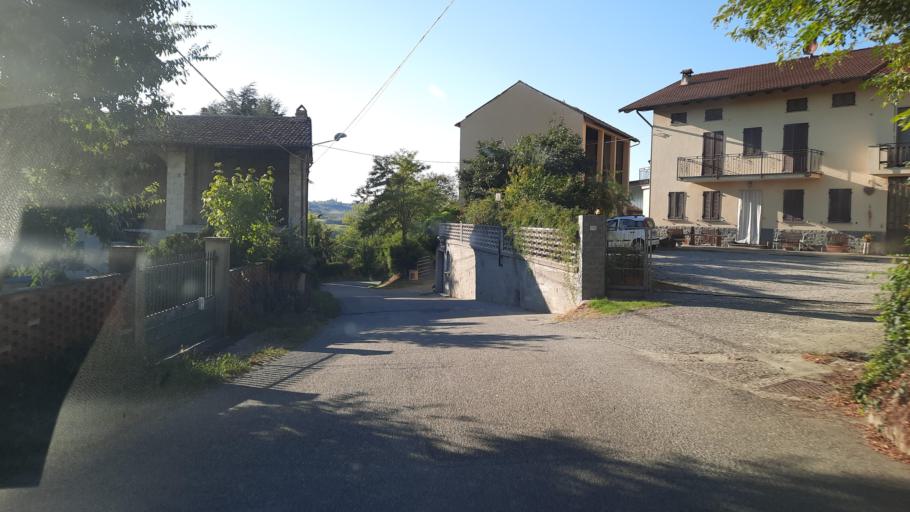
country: IT
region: Piedmont
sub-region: Provincia di Alessandria
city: Cuccaro Monferrato
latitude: 44.9957
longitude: 8.4550
